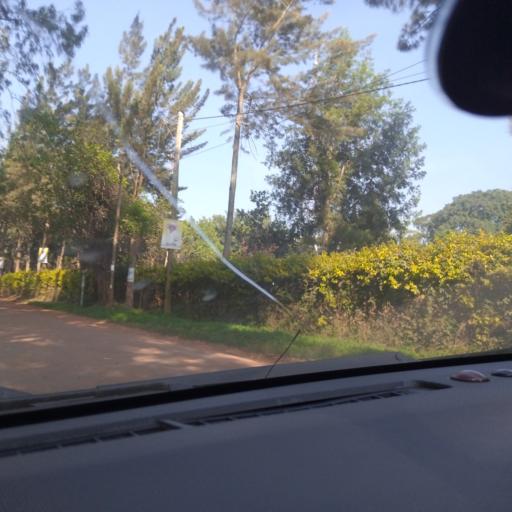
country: UG
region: Central Region
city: Masaka
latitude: -0.3364
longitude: 31.7358
